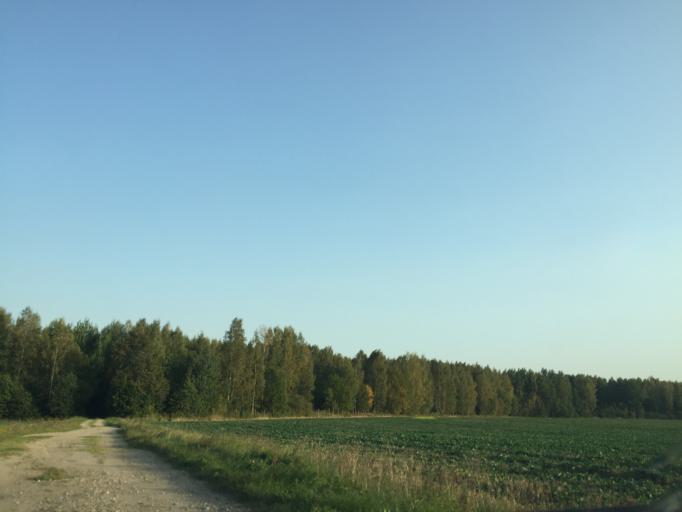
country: LV
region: Lielvarde
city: Lielvarde
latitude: 56.7921
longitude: 24.8256
